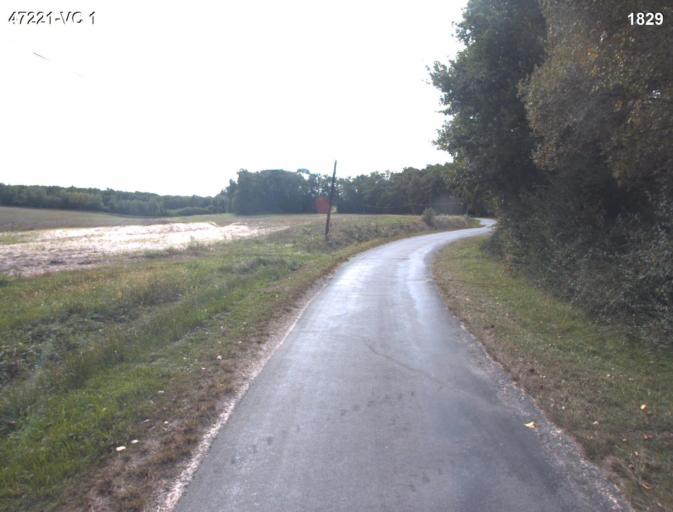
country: FR
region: Aquitaine
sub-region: Departement du Lot-et-Garonne
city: Mezin
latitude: 44.1103
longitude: 0.2392
